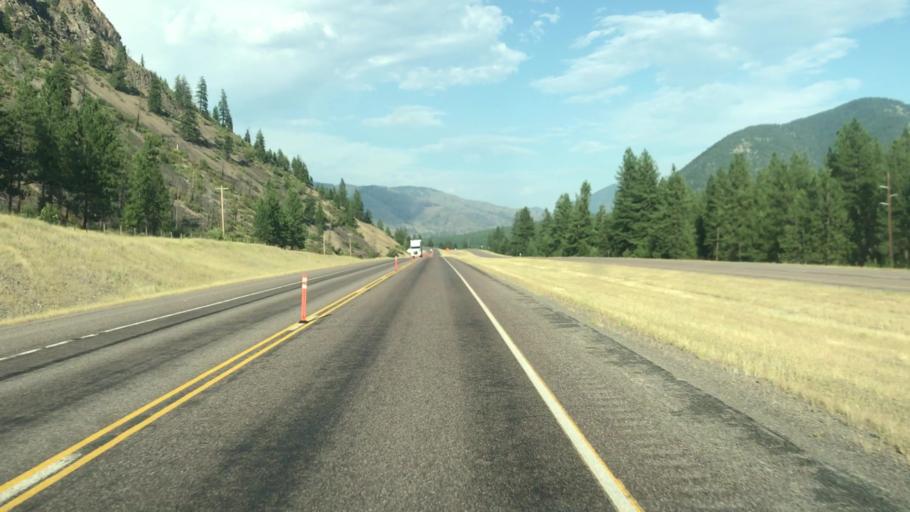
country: US
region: Montana
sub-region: Mineral County
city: Superior
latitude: 47.0124
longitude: -114.7095
